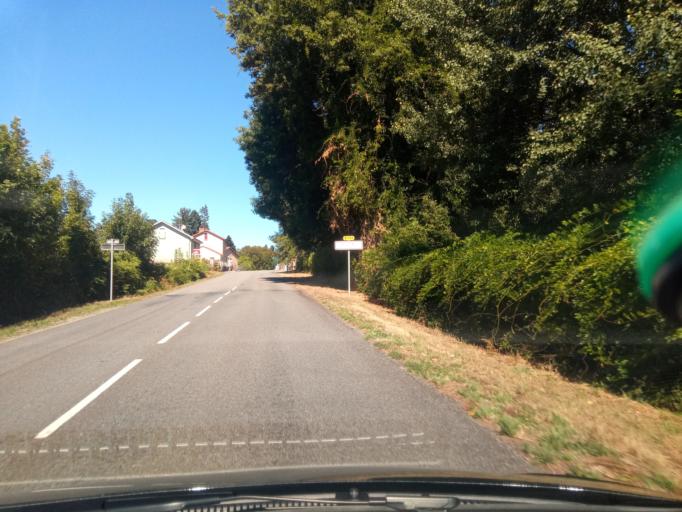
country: FR
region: Limousin
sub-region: Departement de la Haute-Vienne
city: Nantiat
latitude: 46.0734
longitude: 1.2028
